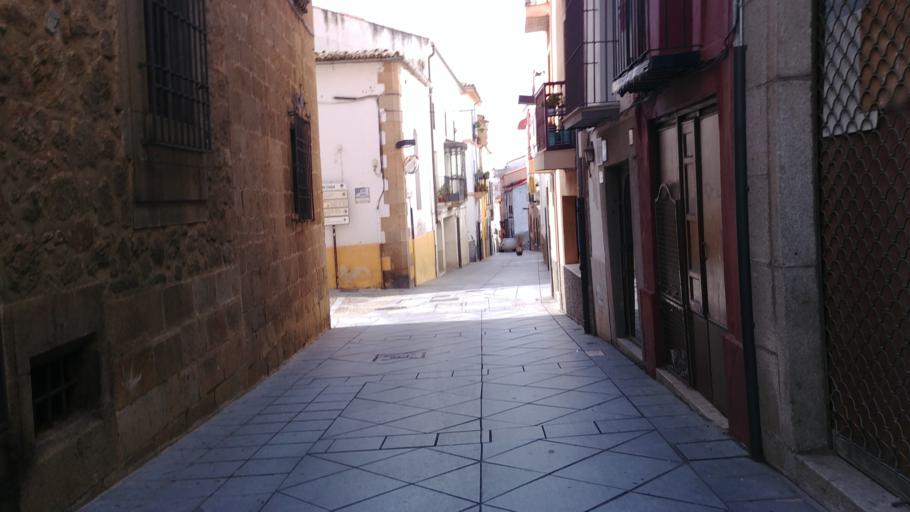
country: ES
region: Extremadura
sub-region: Provincia de Caceres
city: Plasencia
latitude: 40.0285
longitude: -6.0916
